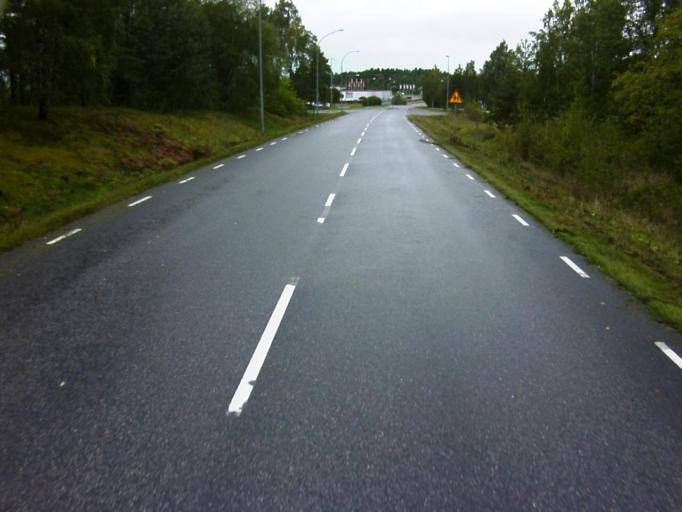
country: SE
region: Soedermanland
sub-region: Eskilstuna Kommun
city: Eskilstuna
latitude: 59.3872
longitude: 16.5422
